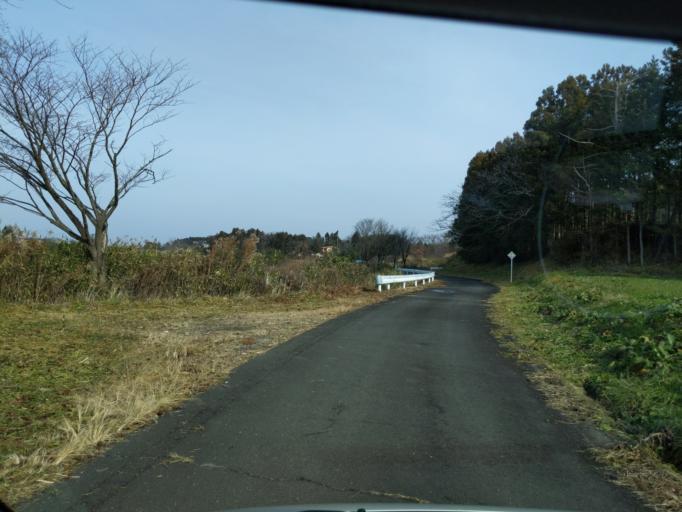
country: JP
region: Miyagi
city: Wakuya
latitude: 38.6976
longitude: 141.1504
